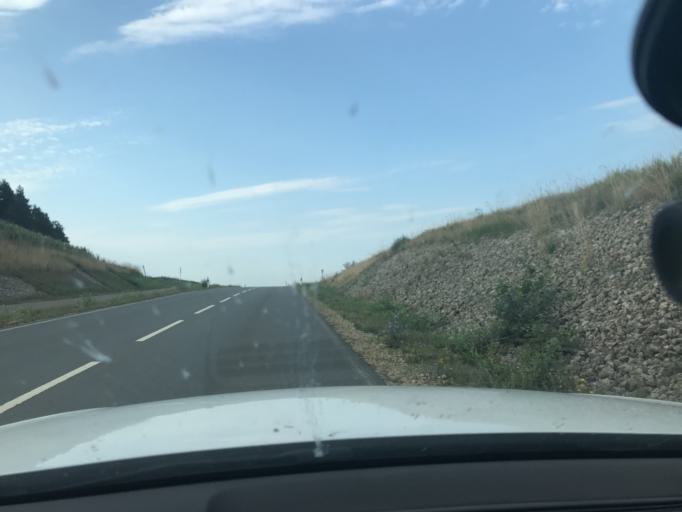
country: DE
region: Bavaria
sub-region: Upper Palatinate
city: Auerbach
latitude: 49.7191
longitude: 11.6183
